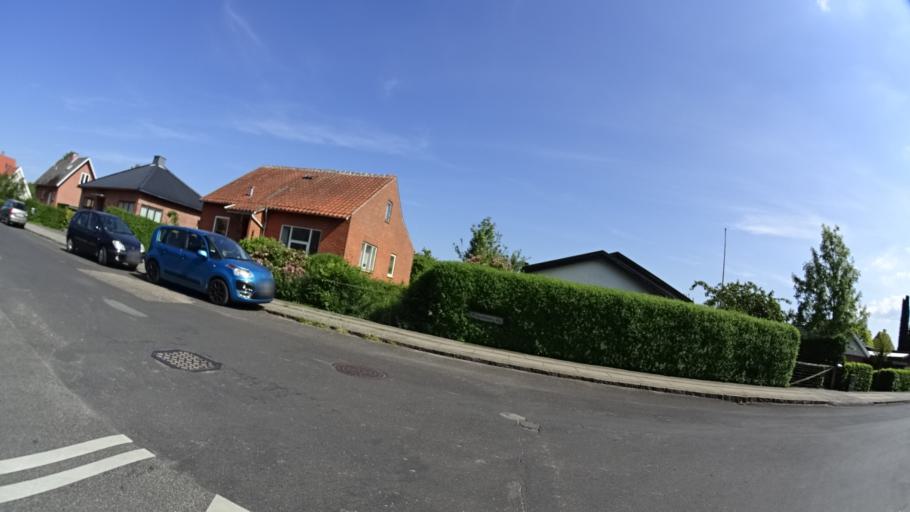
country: DK
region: Central Jutland
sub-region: Arhus Kommune
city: Stavtrup
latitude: 56.1508
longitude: 10.1516
